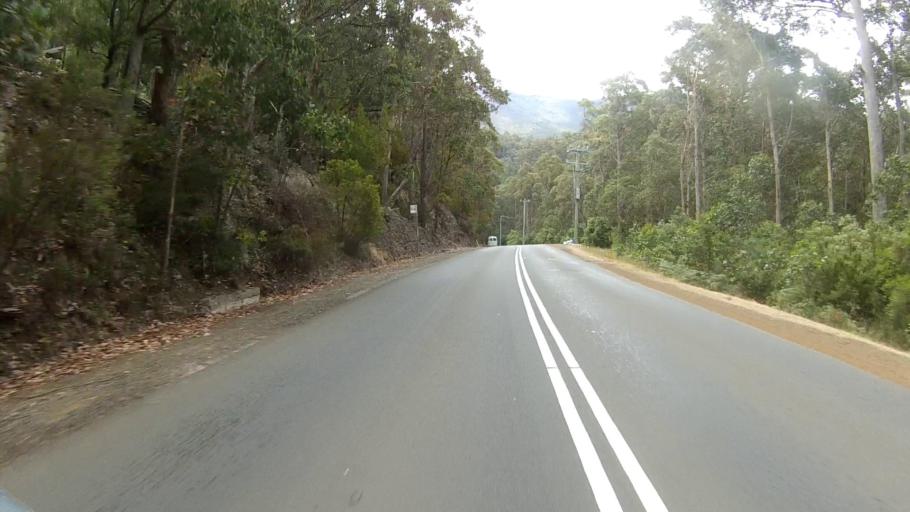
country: AU
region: Tasmania
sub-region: Hobart
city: Dynnyrne
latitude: -42.9163
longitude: 147.2676
